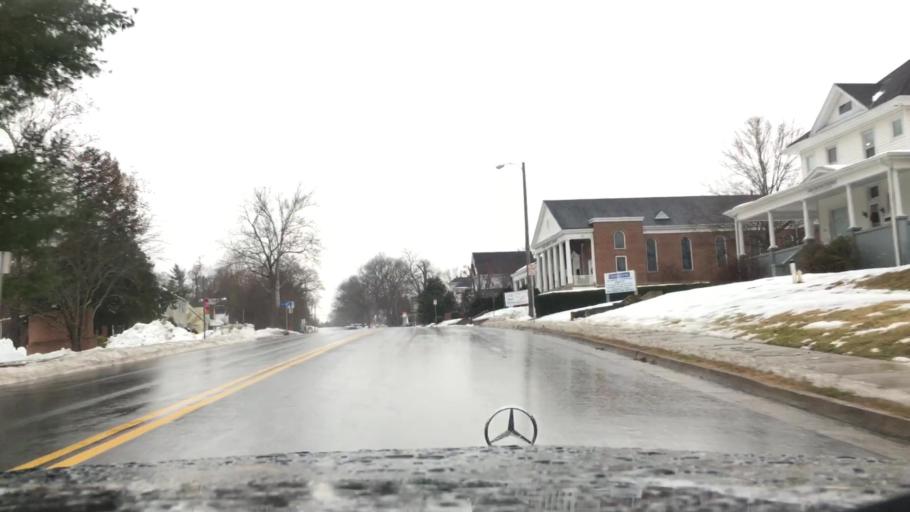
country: US
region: Virginia
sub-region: Campbell County
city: Altavista
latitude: 37.1106
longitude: -79.2947
